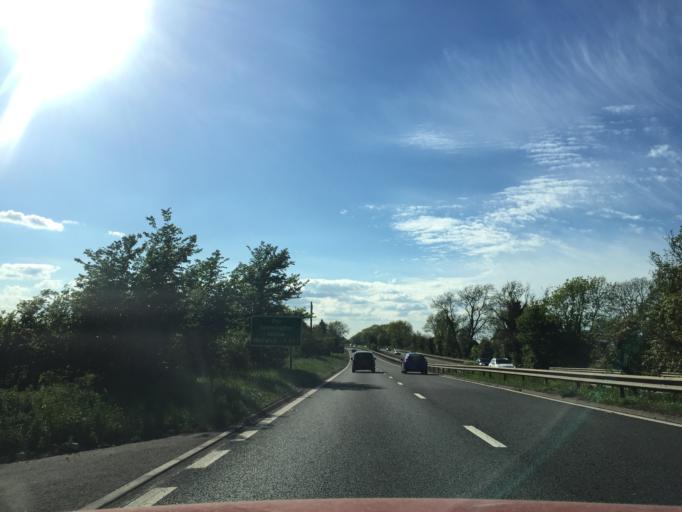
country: GB
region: England
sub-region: Warwickshire
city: Ryton on Dunsmore
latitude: 52.3621
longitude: -1.4138
